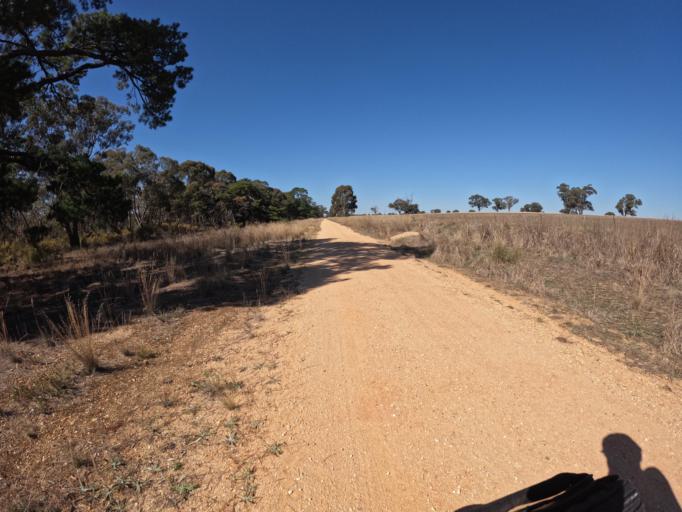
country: AU
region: Victoria
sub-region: Greater Bendigo
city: Kennington
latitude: -36.8348
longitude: 144.5960
